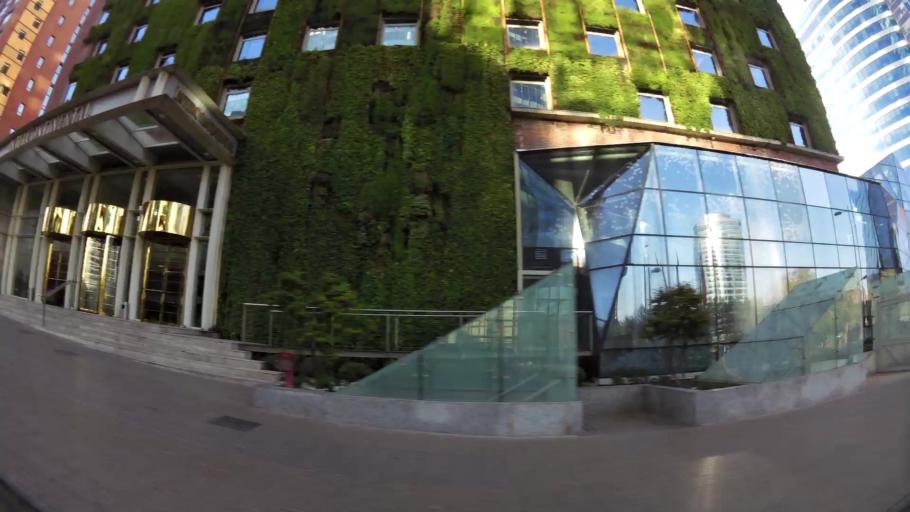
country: CL
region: Santiago Metropolitan
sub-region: Provincia de Santiago
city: Villa Presidente Frei, Nunoa, Santiago, Chile
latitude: -33.4133
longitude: -70.6033
